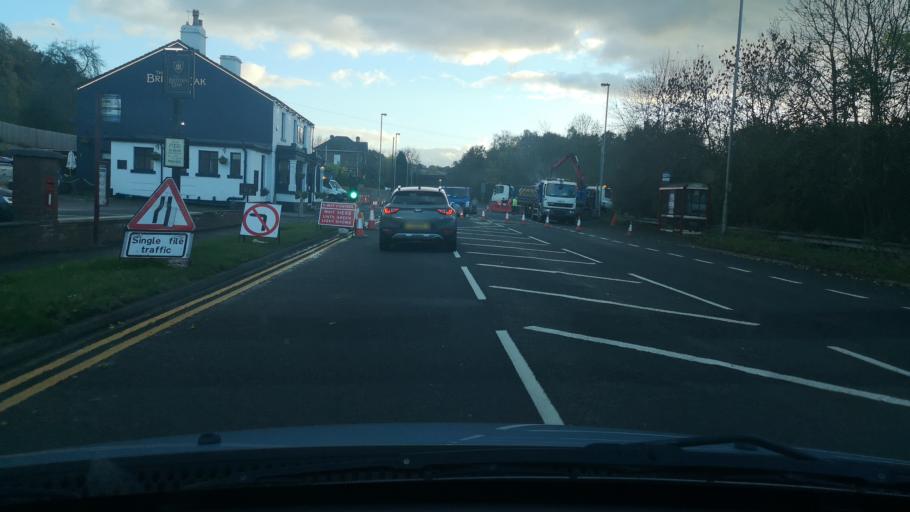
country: GB
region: England
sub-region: City and Borough of Wakefield
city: Crigglestone
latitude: 53.6428
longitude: -1.5466
